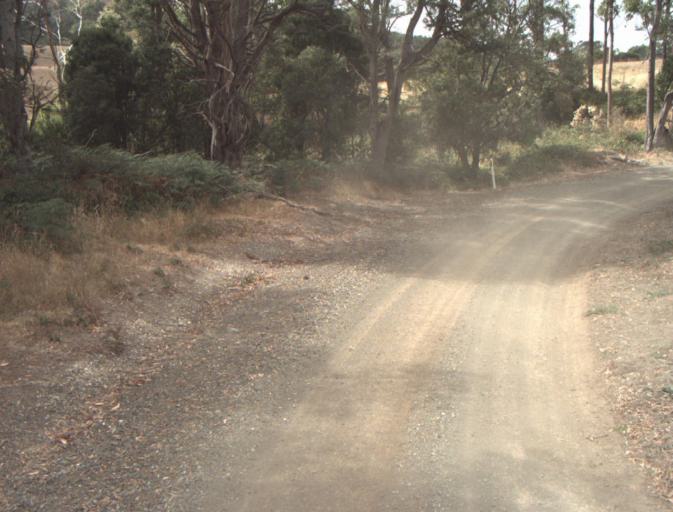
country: AU
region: Tasmania
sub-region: Launceston
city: Mayfield
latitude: -41.1696
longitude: 147.2126
